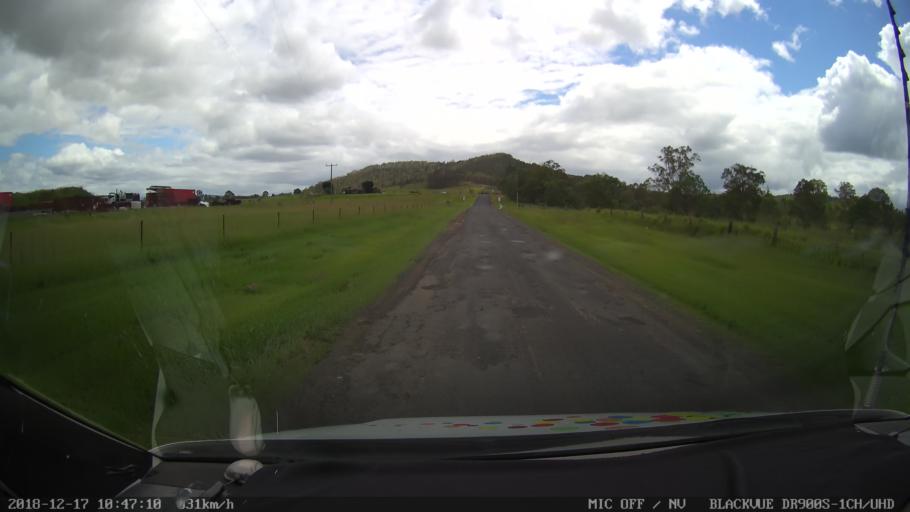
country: AU
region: New South Wales
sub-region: Clarence Valley
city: Gordon
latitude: -28.8819
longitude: 152.5698
